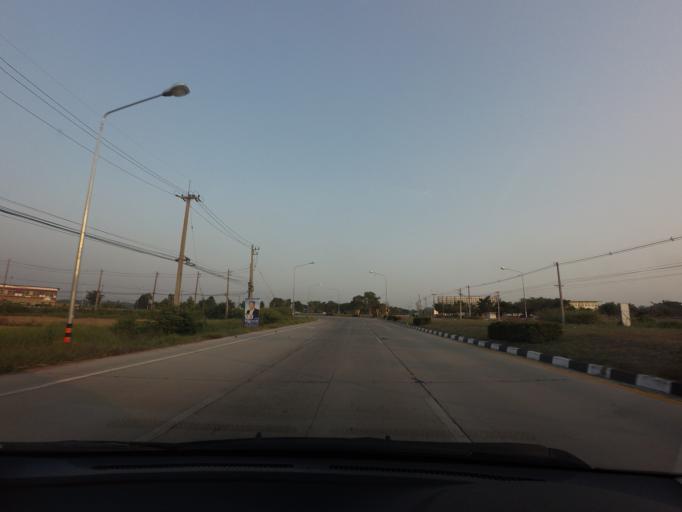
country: TH
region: Sukhothai
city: Kong Krailat
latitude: 17.0078
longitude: 99.9282
